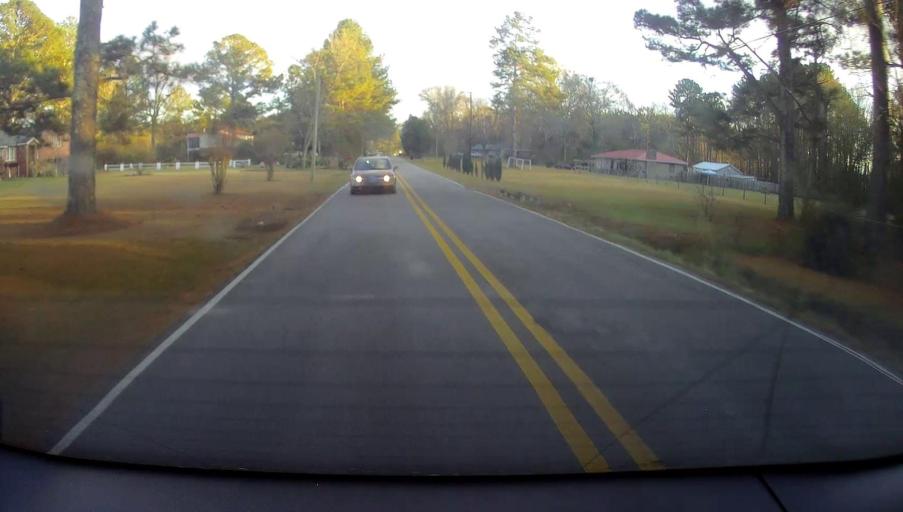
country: US
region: Alabama
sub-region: Etowah County
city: Gadsden
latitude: 33.9769
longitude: -85.9806
